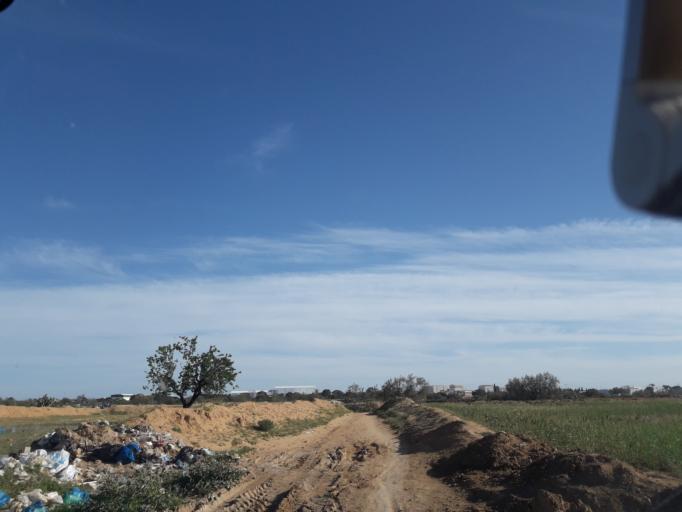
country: TN
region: Safaqis
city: Sfax
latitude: 34.7358
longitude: 10.5176
